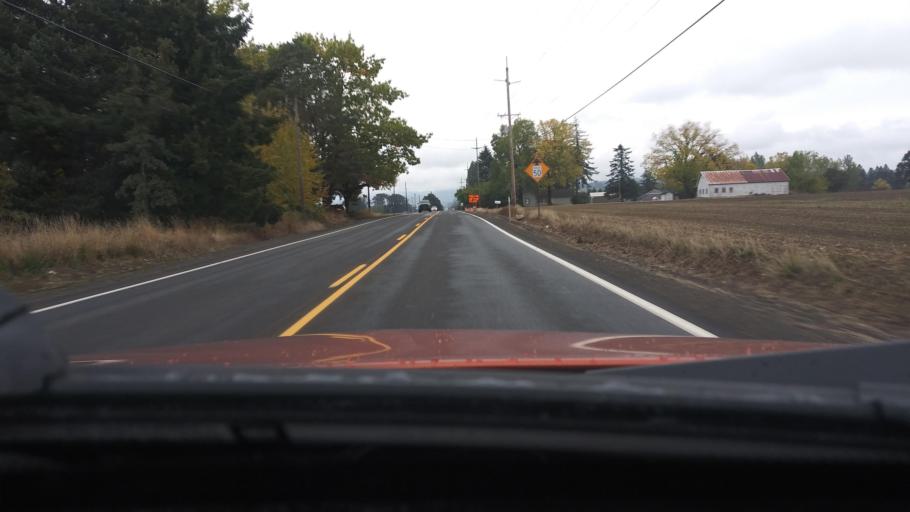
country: US
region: Oregon
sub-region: Washington County
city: Banks
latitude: 45.6002
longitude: -123.1145
